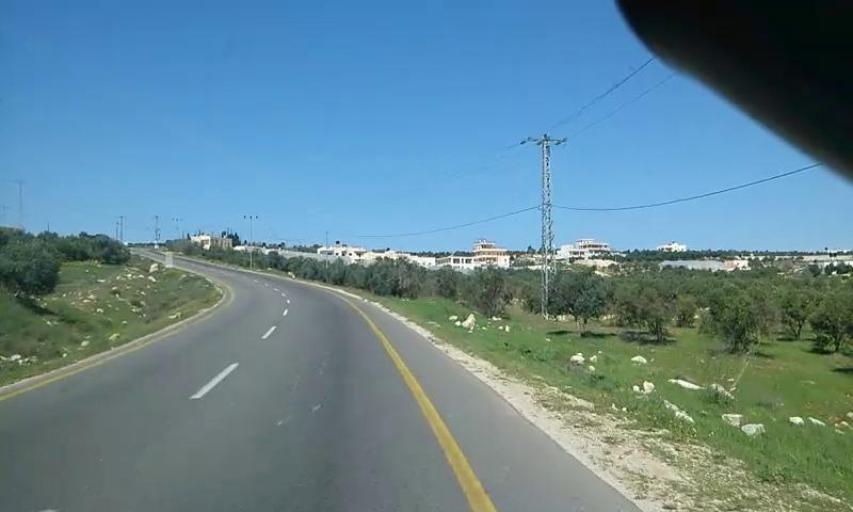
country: PS
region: West Bank
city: Marah Rabbah
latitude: 31.6440
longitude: 35.1936
